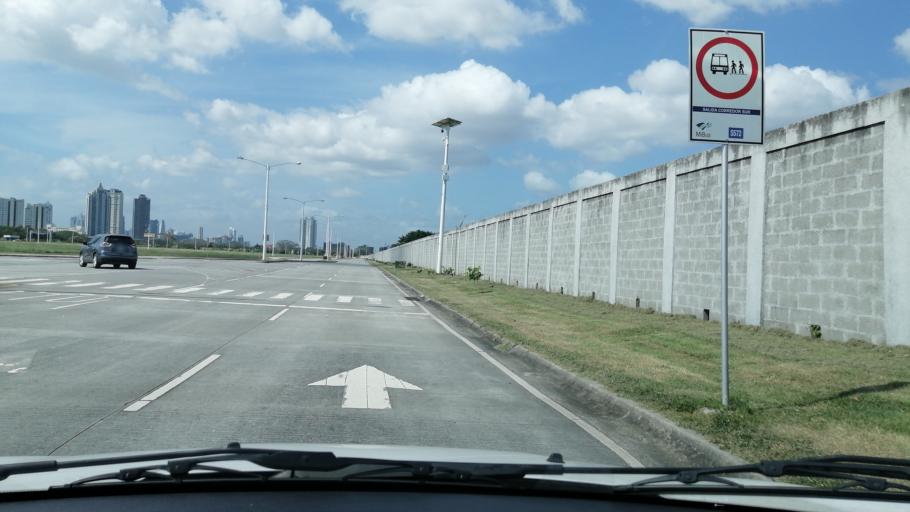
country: PA
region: Panama
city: San Miguelito
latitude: 9.0368
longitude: -79.4405
